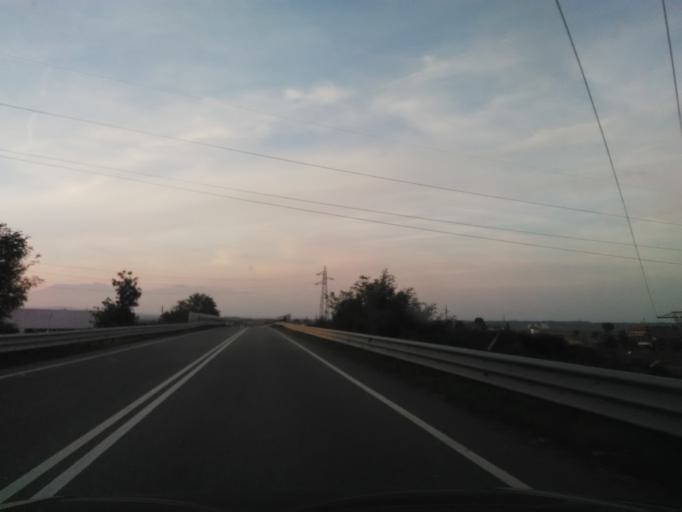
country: IT
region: Piedmont
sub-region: Provincia di Vercelli
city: Santhia
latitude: 45.3658
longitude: 8.1860
